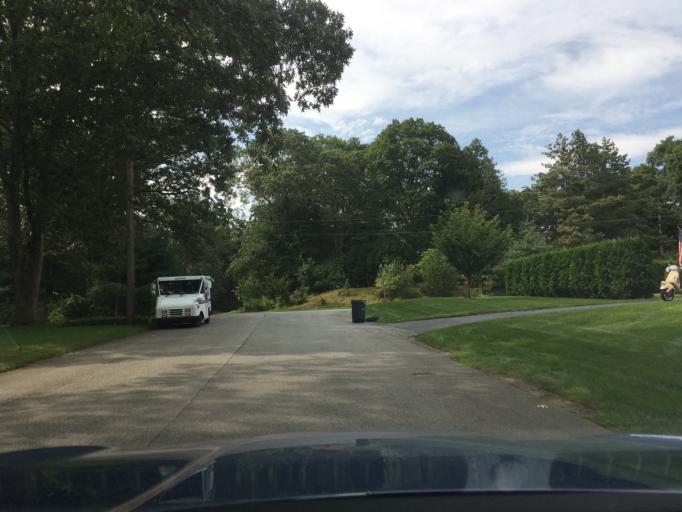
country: US
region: Rhode Island
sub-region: Kent County
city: East Greenwich
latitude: 41.6565
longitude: -71.4686
